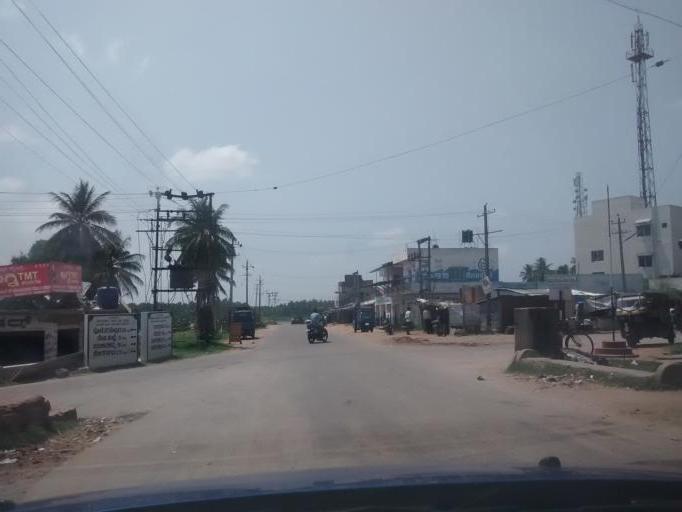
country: IN
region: Karnataka
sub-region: Hassan
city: Konanur
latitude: 12.5630
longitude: 76.2635
